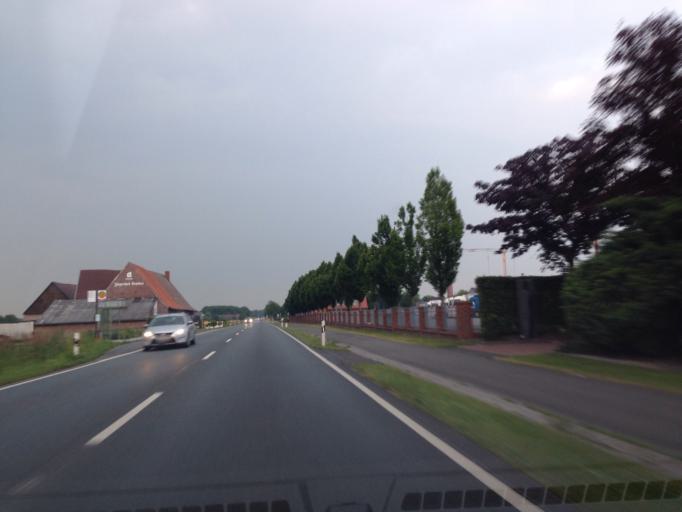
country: DE
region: North Rhine-Westphalia
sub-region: Regierungsbezirk Munster
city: Nottuln
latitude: 51.9166
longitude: 7.3838
